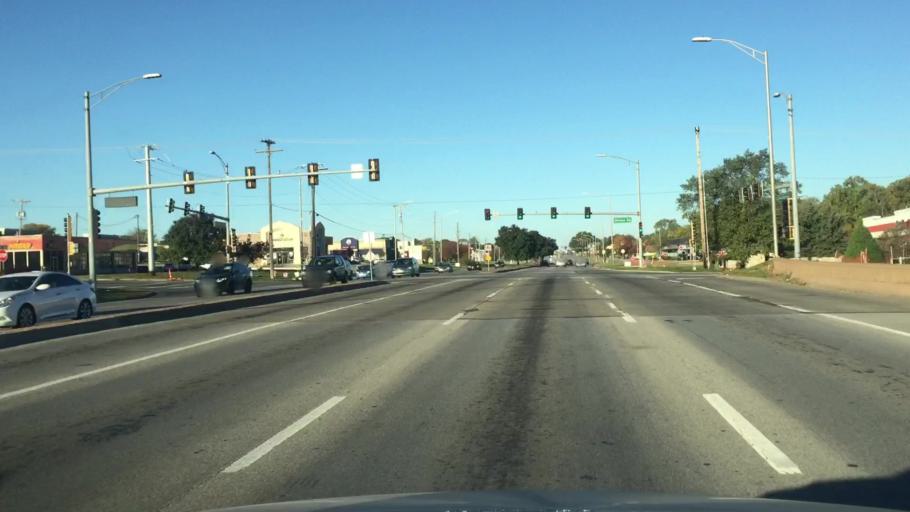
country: US
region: Kansas
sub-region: Johnson County
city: Merriam
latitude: 39.0149
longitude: -94.7138
